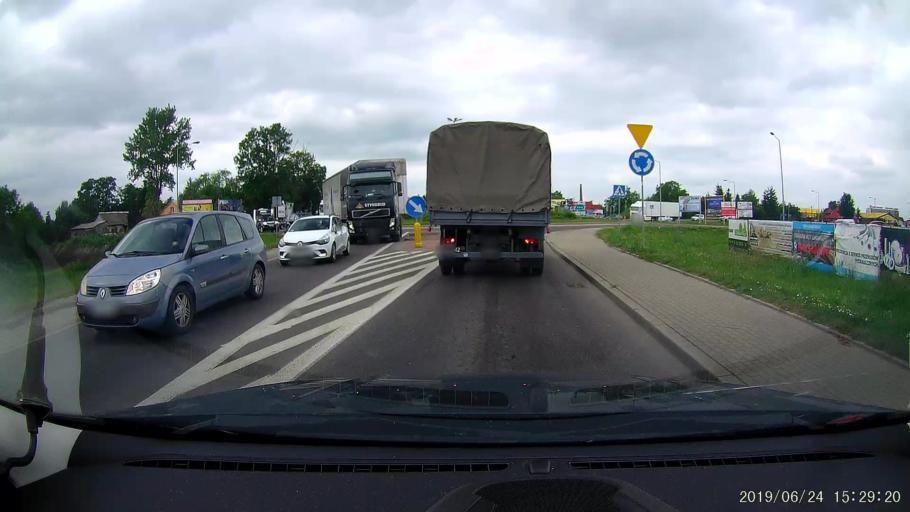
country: PL
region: Subcarpathian Voivodeship
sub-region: Powiat jaroslawski
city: Jaroslaw
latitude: 50.0258
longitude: 22.7149
